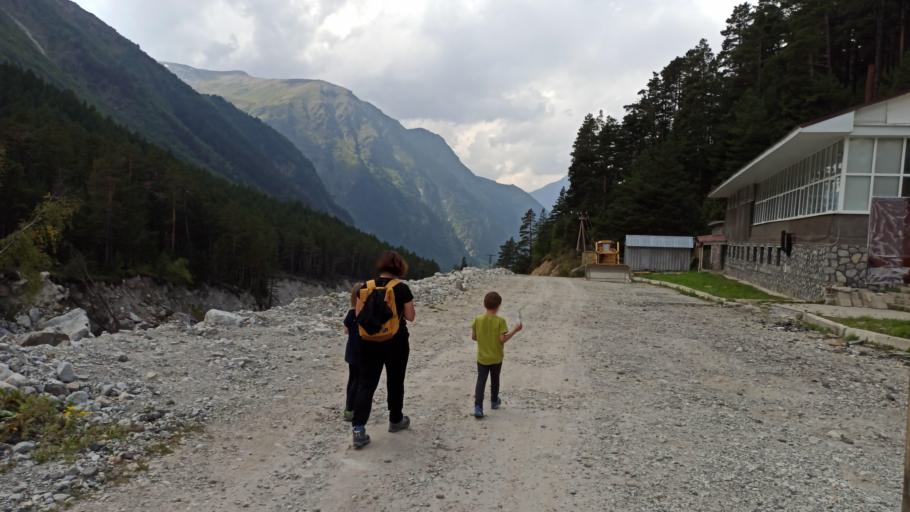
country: RU
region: Kabardino-Balkariya
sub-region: El'brusskiy Rayon
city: El'brus
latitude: 43.2192
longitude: 42.6914
